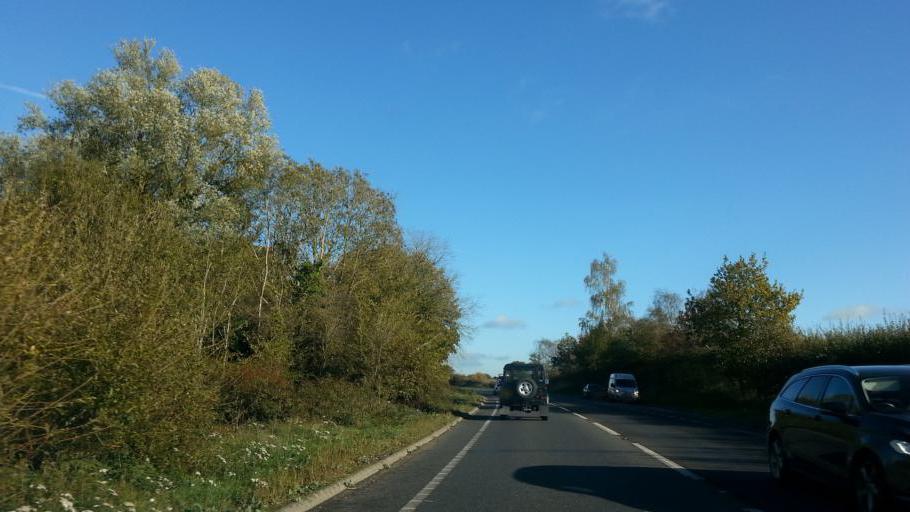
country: GB
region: England
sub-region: Norfolk
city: Harleston
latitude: 52.4132
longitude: 1.3334
